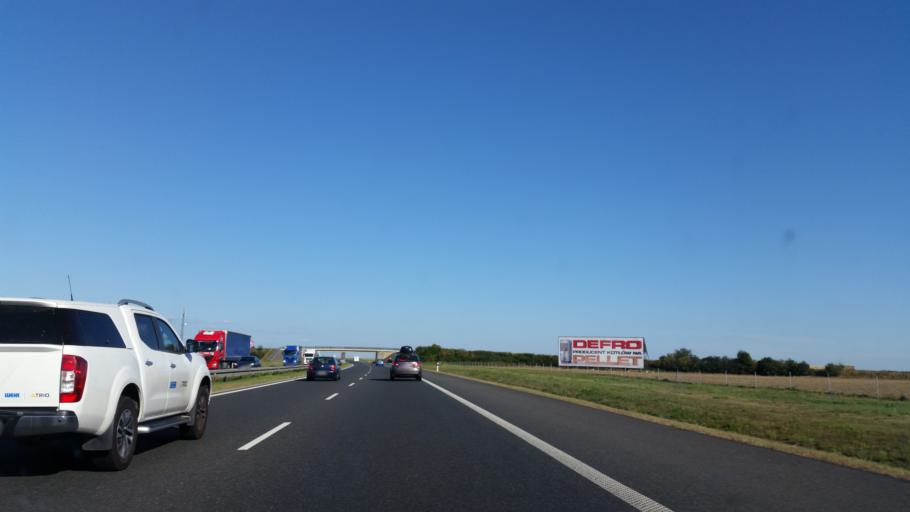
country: PL
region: Opole Voivodeship
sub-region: Powiat brzeski
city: Olszanka
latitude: 50.7392
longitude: 17.4667
